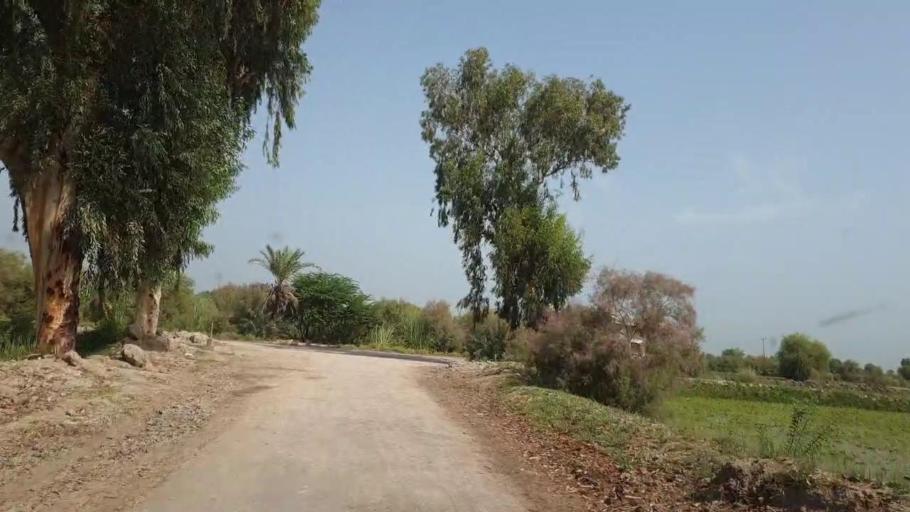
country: PK
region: Sindh
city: Lakhi
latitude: 27.8356
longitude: 68.6805
